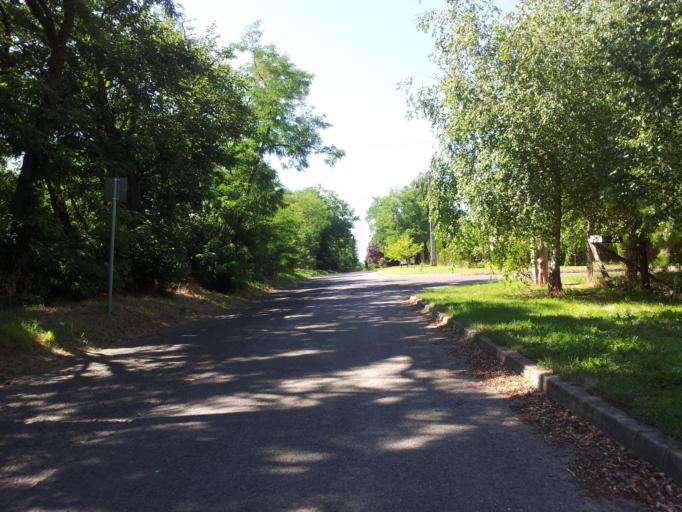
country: HU
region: Pest
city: Veresegyhaz
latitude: 47.6513
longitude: 19.2615
